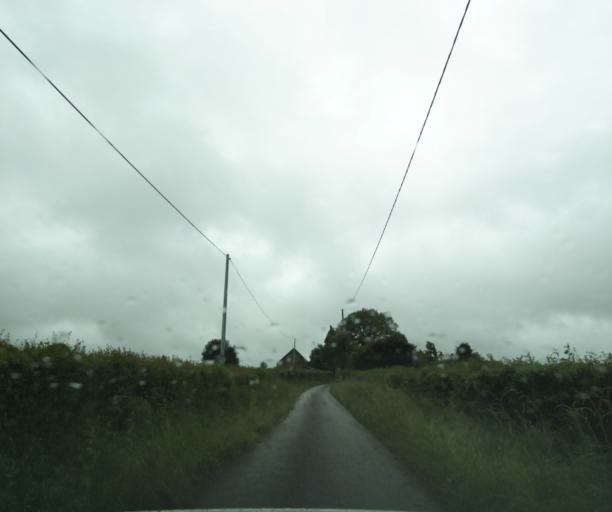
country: FR
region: Bourgogne
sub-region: Departement de Saone-et-Loire
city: Charolles
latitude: 46.4990
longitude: 4.3959
